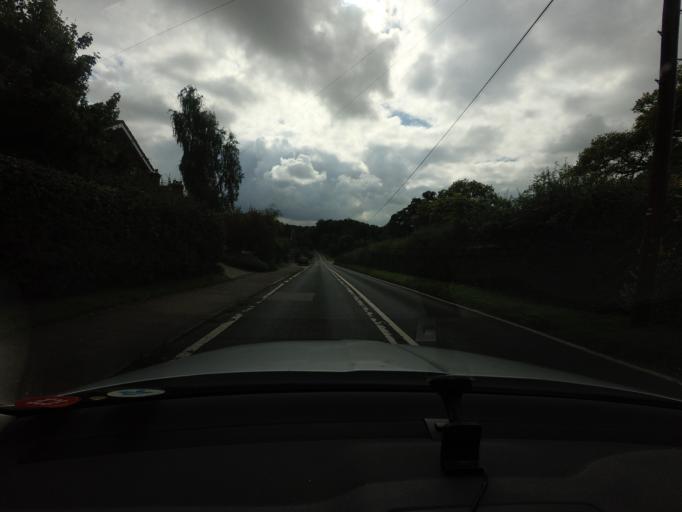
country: GB
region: England
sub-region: Kent
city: Tonbridge
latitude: 51.2450
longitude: 0.2792
